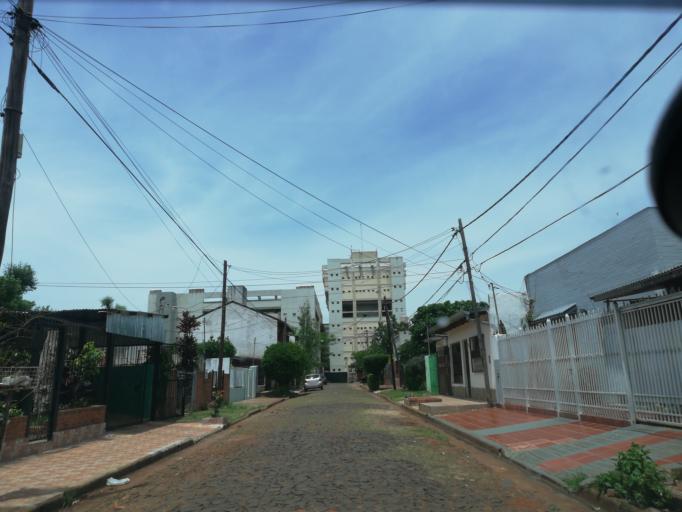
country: AR
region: Misiones
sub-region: Departamento de Capital
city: Posadas
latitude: -27.3640
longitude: -55.9078
